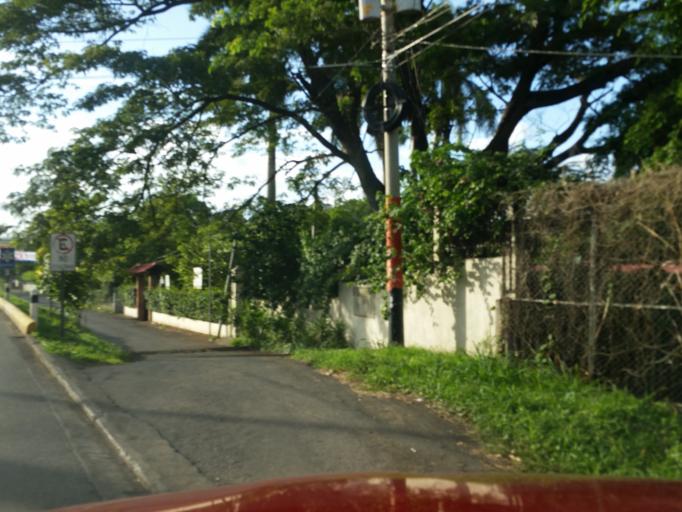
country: NI
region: Managua
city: Managua
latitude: 12.0861
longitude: -86.2304
